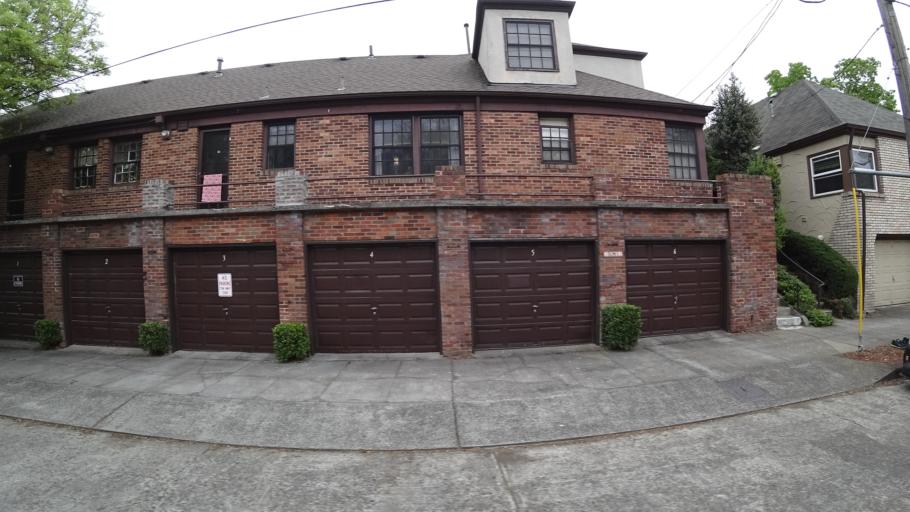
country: US
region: Oregon
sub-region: Multnomah County
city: Portland
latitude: 45.5218
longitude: -122.6331
